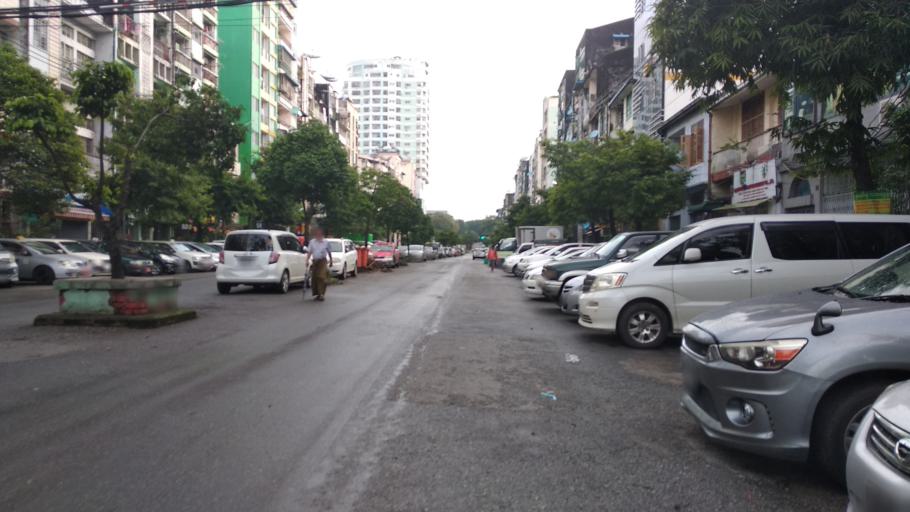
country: MM
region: Yangon
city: Yangon
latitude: 16.7752
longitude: 96.1421
